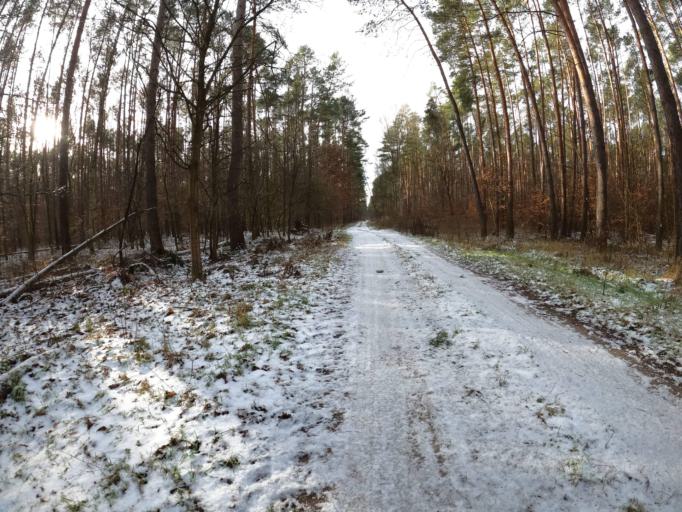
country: PL
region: Lubusz
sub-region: Powiat slubicki
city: Rzepin
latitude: 52.2910
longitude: 14.8178
